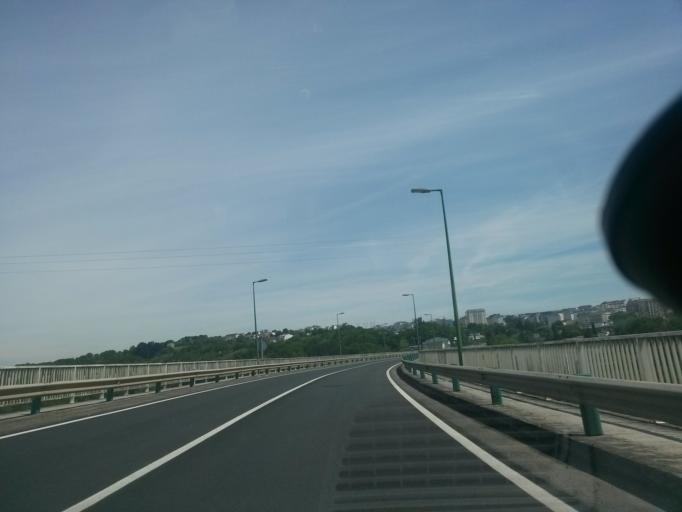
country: ES
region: Galicia
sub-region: Provincia de Lugo
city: Lugo
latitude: 43.0046
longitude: -7.5828
